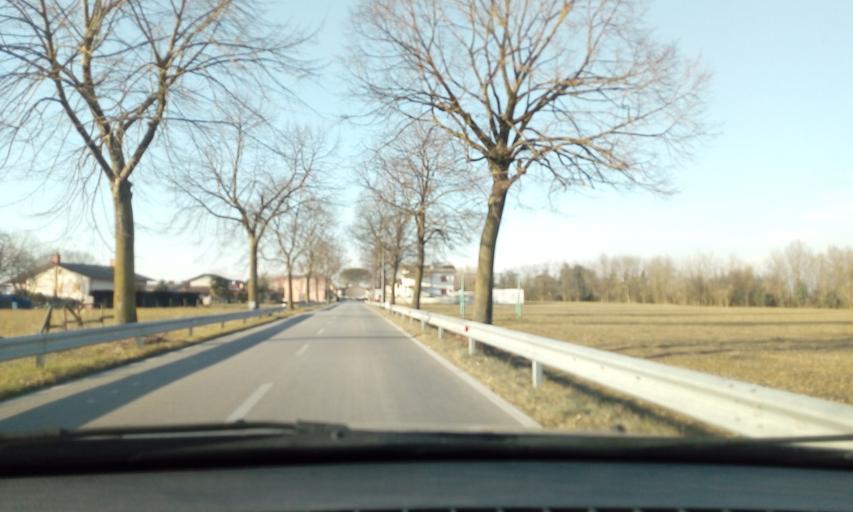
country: IT
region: Friuli Venezia Giulia
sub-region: Provincia di Udine
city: Chiopris
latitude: 45.9200
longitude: 13.4064
